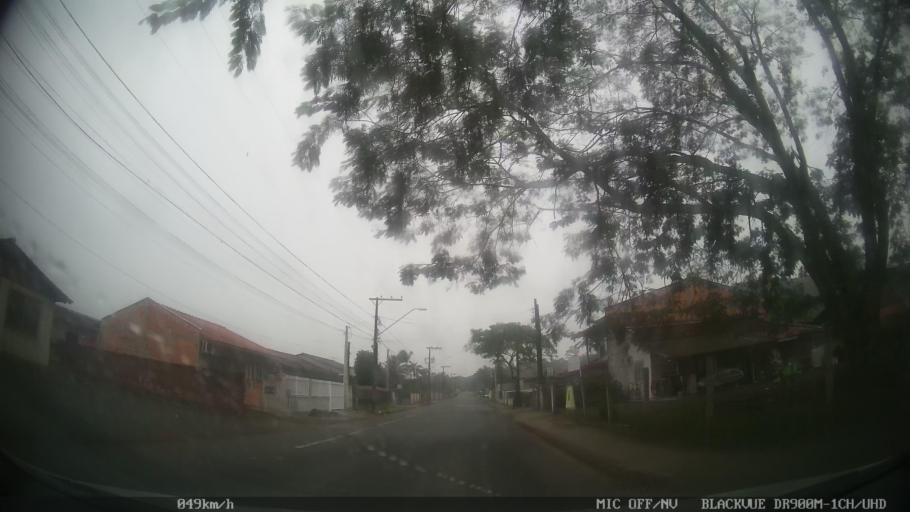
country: BR
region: Santa Catarina
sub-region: Joinville
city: Joinville
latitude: -26.2120
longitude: -48.8275
